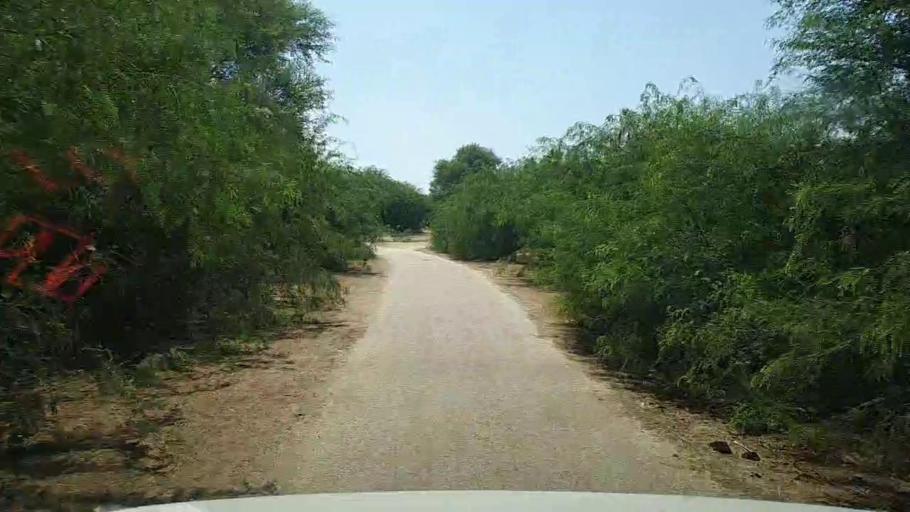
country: PK
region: Sindh
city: Kandhkot
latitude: 28.2868
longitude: 69.3538
